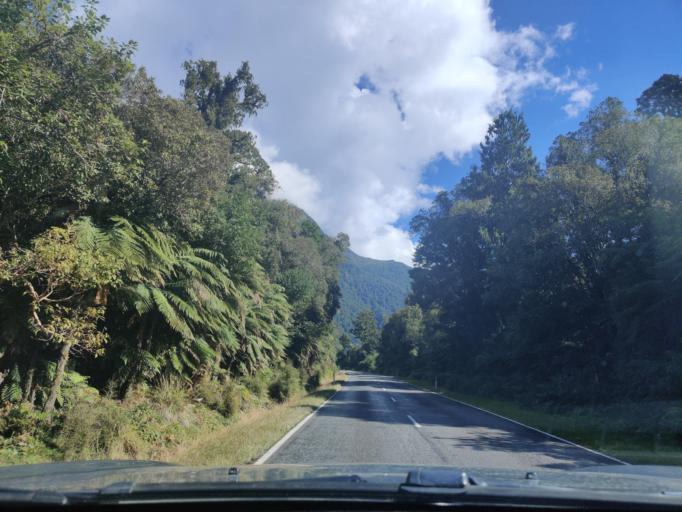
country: NZ
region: Otago
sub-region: Queenstown-Lakes District
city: Wanaka
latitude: -43.9682
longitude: 169.1756
